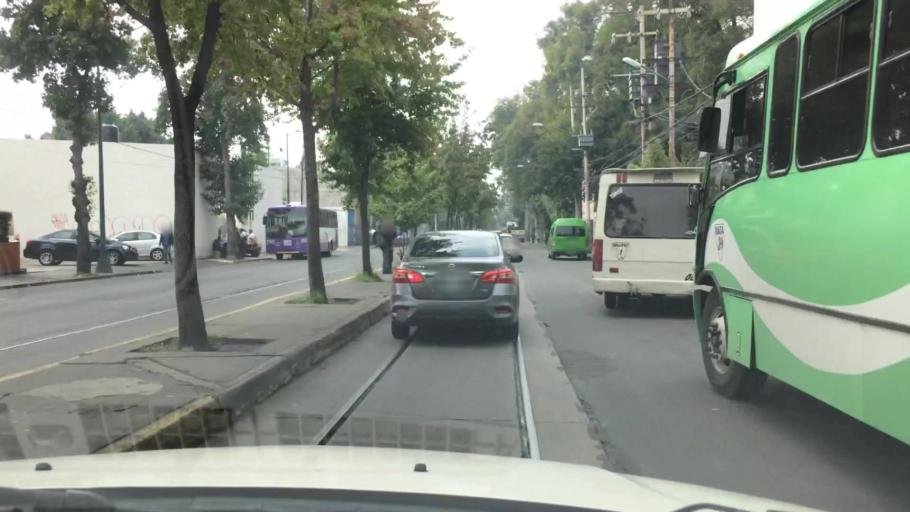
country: MX
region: Mexico City
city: Tlalpan
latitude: 19.2978
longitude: -99.1525
